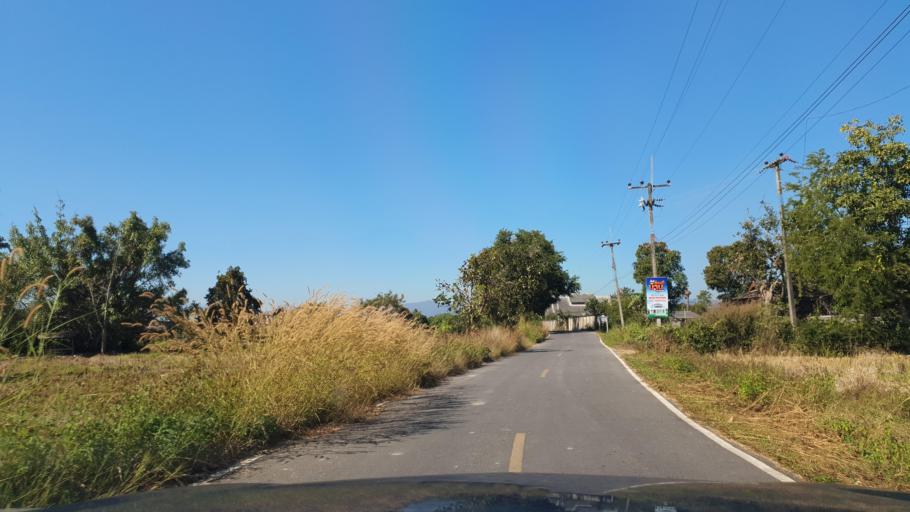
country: TH
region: Chiang Mai
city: San Pa Tong
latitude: 18.6500
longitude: 98.8931
